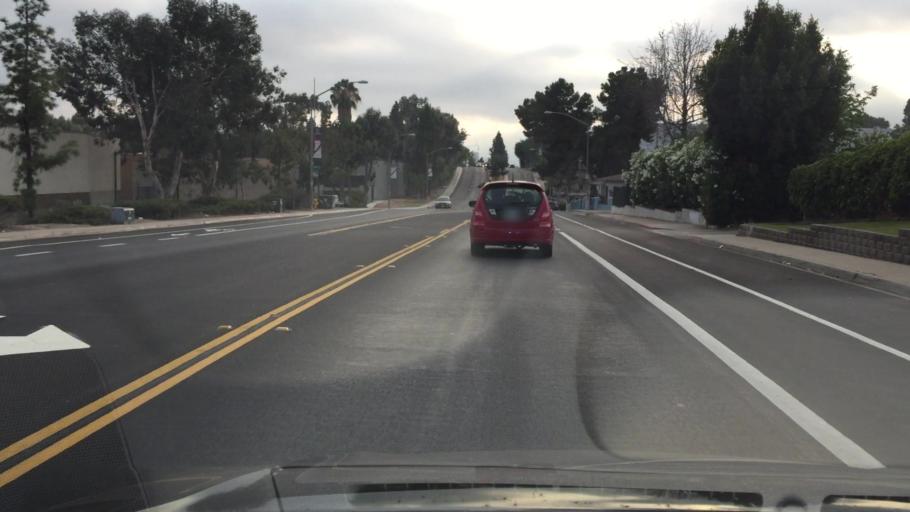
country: US
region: California
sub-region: San Diego County
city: National City
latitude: 32.7115
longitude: -117.1079
